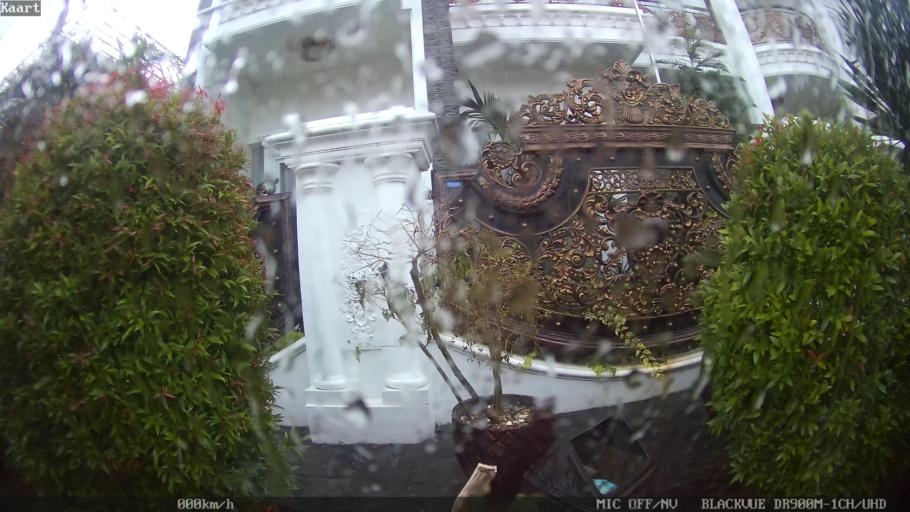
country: ID
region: Lampung
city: Kedaton
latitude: -5.3964
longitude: 105.2860
